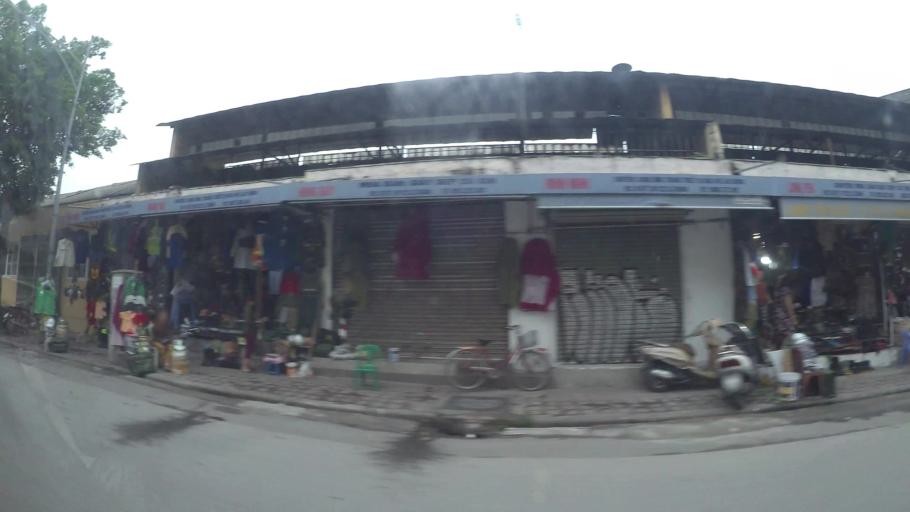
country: VN
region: Ha Noi
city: Hanoi
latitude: 21.0225
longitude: 105.8414
